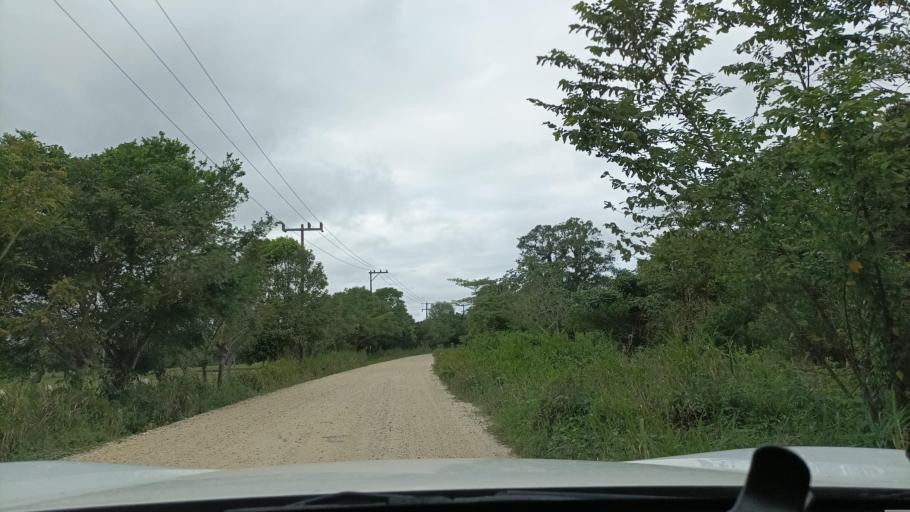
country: MX
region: Veracruz
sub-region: Moloacan
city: Cuichapa
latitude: 17.8456
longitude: -94.3608
